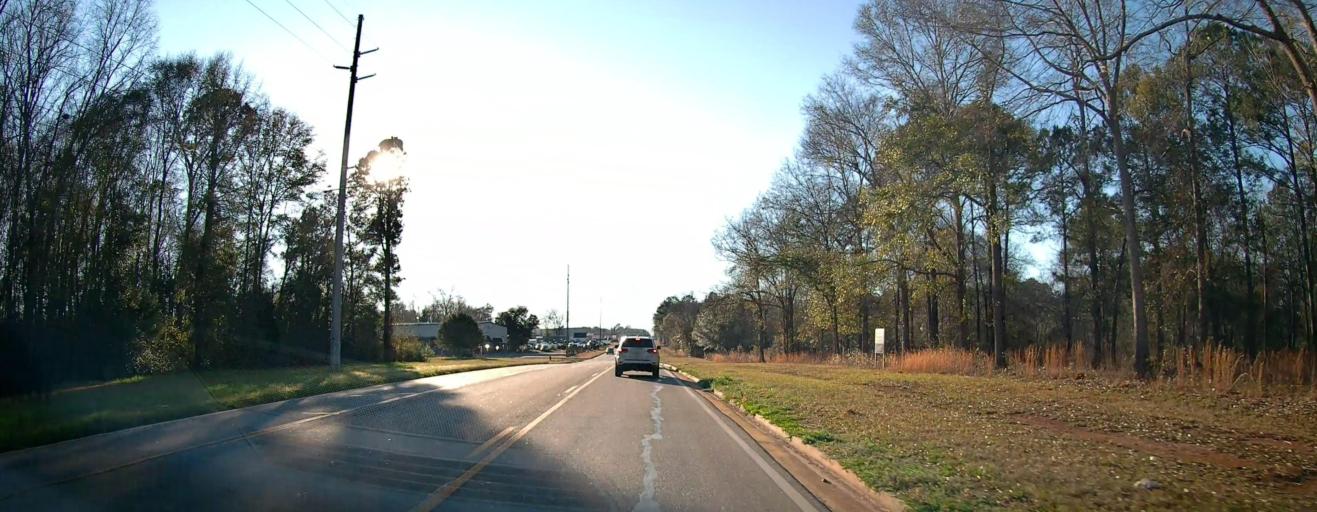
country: US
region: Georgia
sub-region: Dougherty County
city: Albany
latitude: 31.6229
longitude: -84.1829
